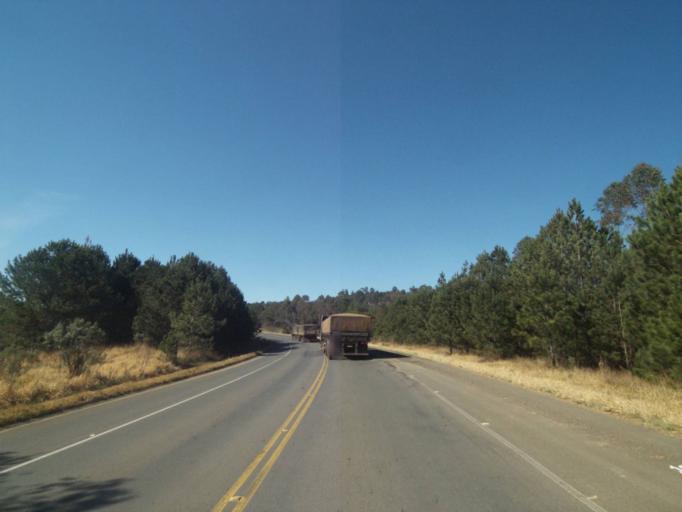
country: BR
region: Parana
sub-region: Tibagi
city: Tibagi
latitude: -24.5787
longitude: -50.4491
